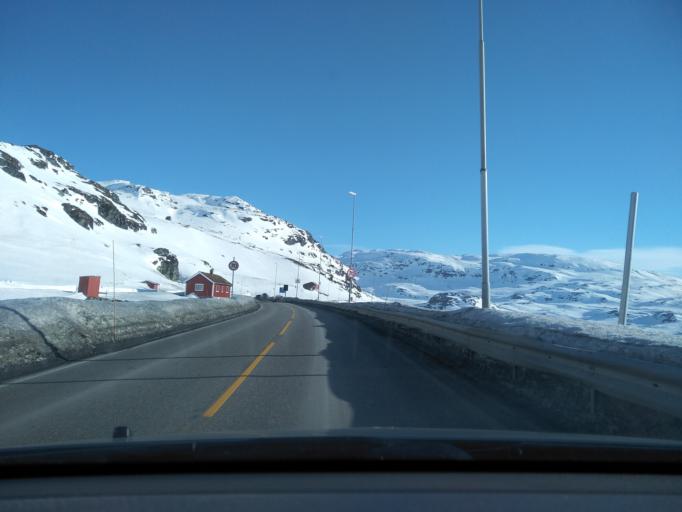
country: NO
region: Aust-Agder
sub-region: Bykle
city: Hovden
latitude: 59.8398
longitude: 6.9856
